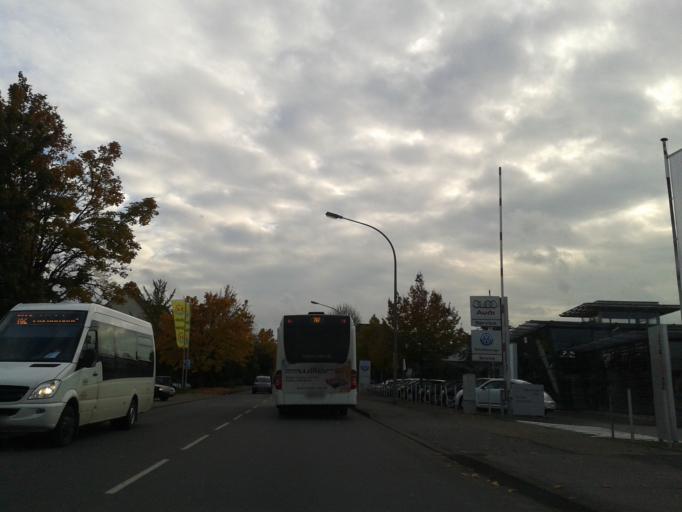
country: DE
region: North Rhine-Westphalia
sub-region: Regierungsbezirk Detmold
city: Horn
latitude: 51.8775
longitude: 8.9534
